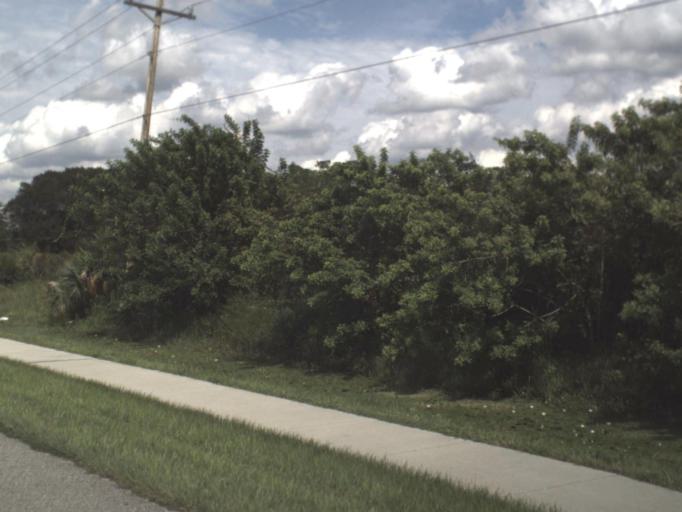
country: US
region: Florida
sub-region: Collier County
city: Immokalee
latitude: 26.5351
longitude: -81.4354
